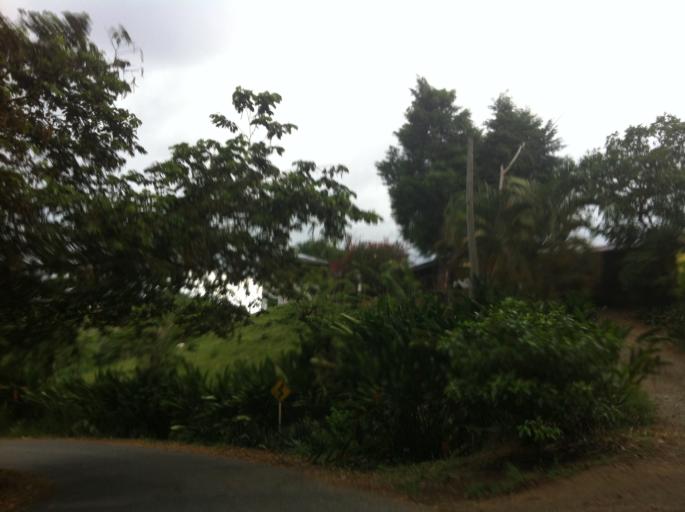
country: CO
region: Quindio
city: Buenavista
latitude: 4.3675
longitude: -75.7583
